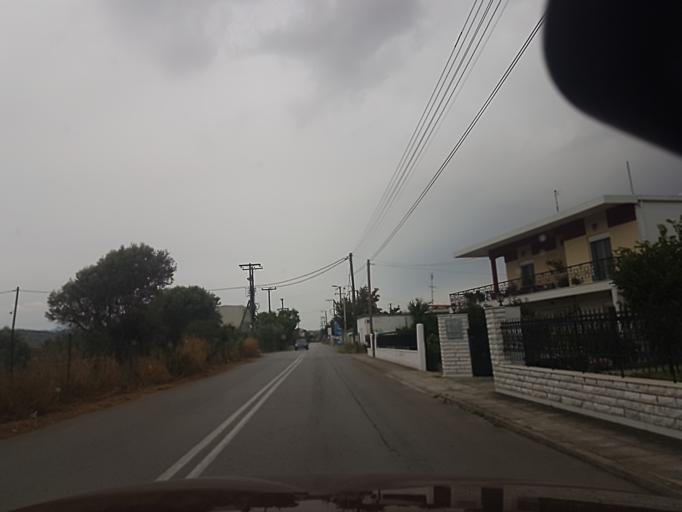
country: GR
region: Central Greece
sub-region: Nomos Evvoias
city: Mytikas
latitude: 38.4645
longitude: 23.6335
